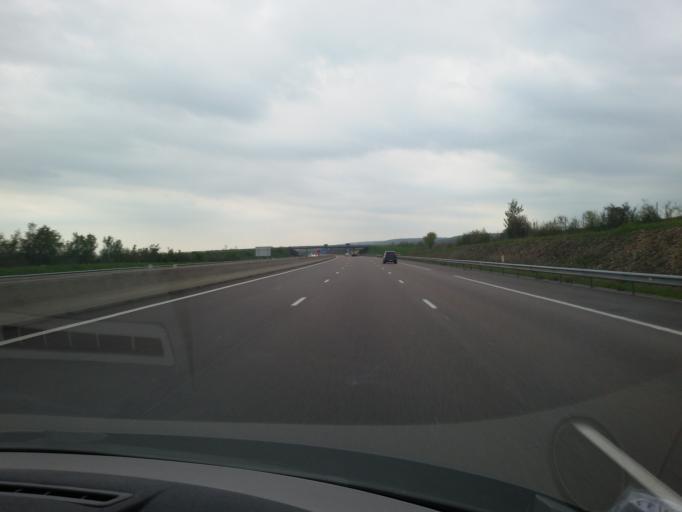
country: FR
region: Champagne-Ardenne
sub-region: Departement de la Haute-Marne
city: Rolampont
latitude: 47.8942
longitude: 5.2242
